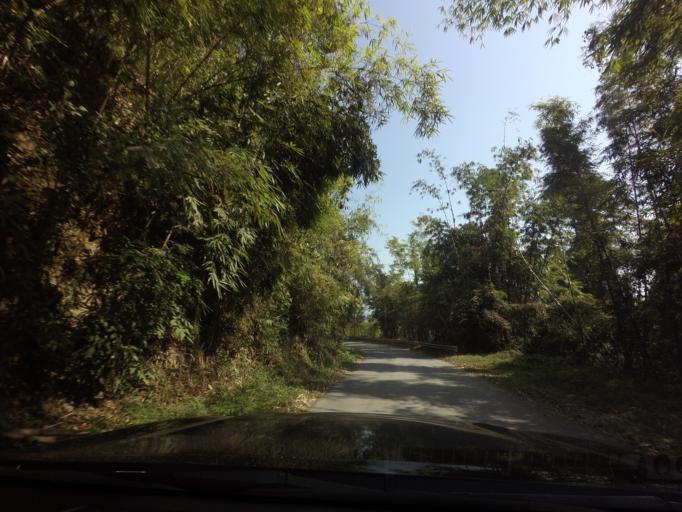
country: TH
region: Kanchanaburi
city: Thong Pha Phum
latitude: 14.6975
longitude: 98.4581
